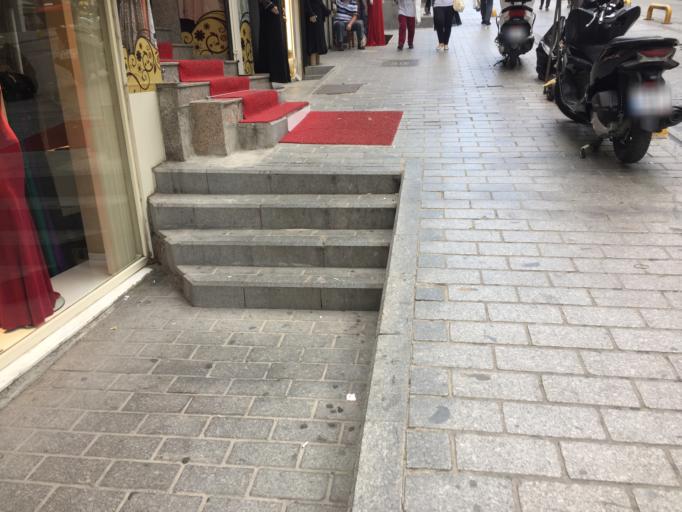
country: TR
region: Istanbul
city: Eminoenue
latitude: 41.0081
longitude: 28.9640
